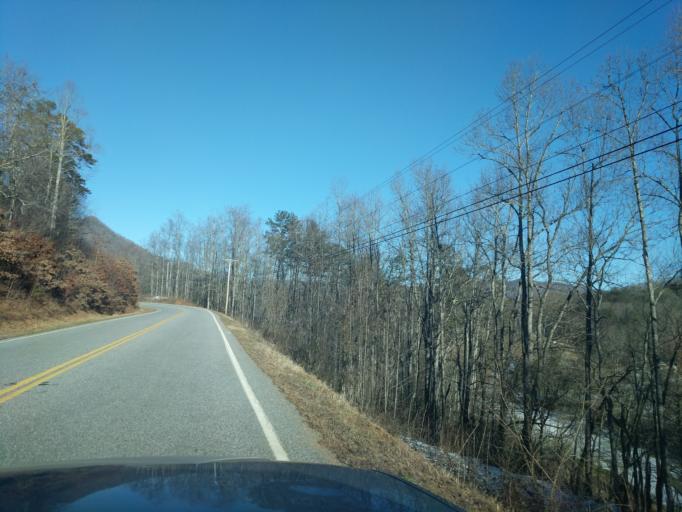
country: US
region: Georgia
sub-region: Towns County
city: Hiawassee
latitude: 34.9244
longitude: -83.6705
